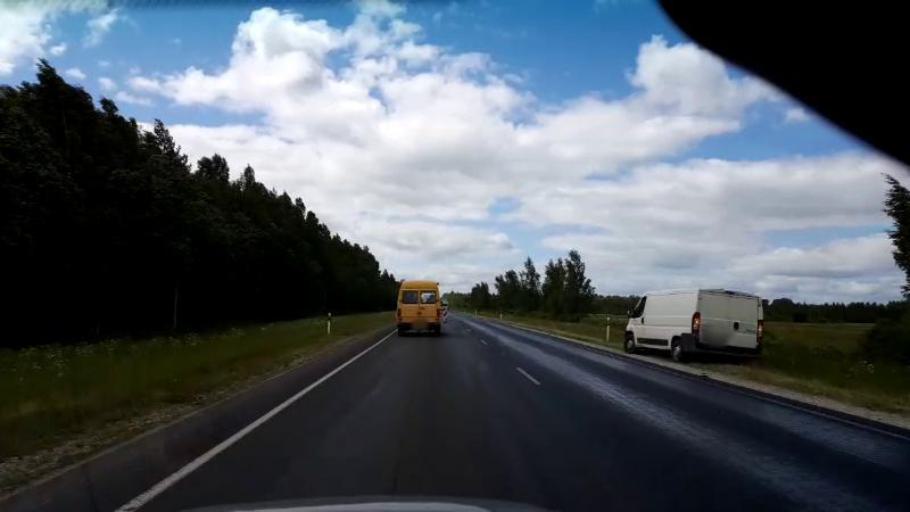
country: LV
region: Salacgrivas
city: Ainazi
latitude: 57.9987
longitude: 24.4780
